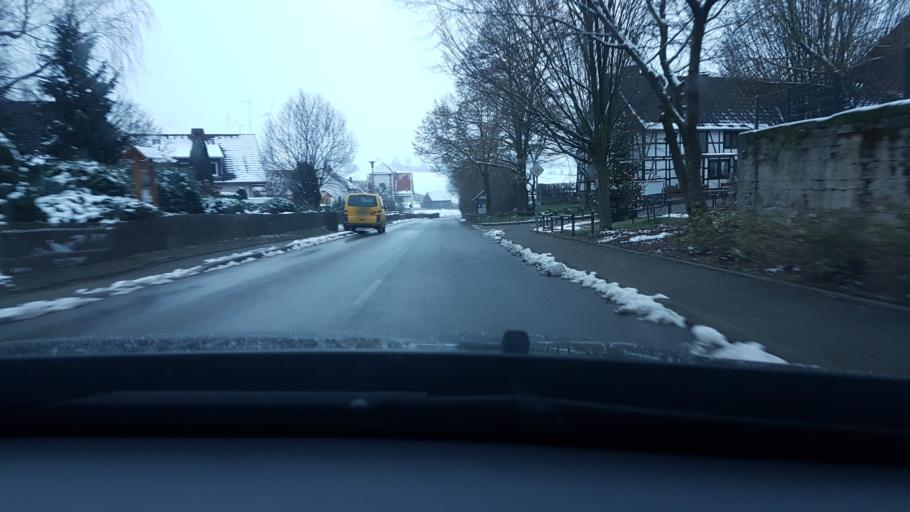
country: DE
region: North Rhine-Westphalia
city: Marsberg
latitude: 51.3838
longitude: 8.8926
